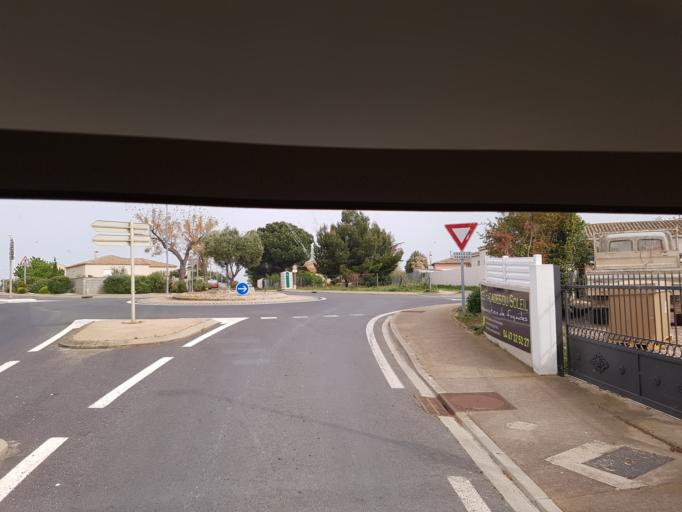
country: FR
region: Languedoc-Roussillon
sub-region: Departement de l'Herault
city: Vendres
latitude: 43.2694
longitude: 3.2281
